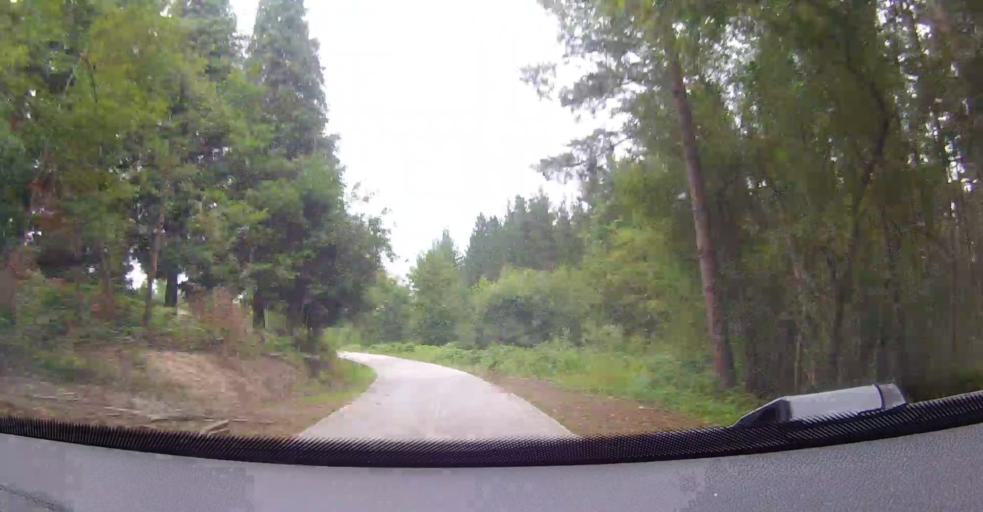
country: ES
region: Basque Country
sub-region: Bizkaia
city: Urrestieta
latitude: 43.2300
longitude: -3.1762
